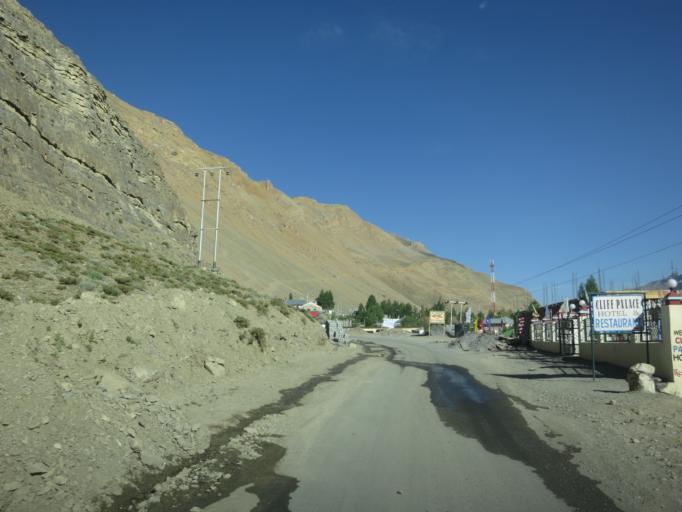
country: IN
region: Himachal Pradesh
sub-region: Shimla
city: Sarahan
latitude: 32.2301
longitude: 78.0670
